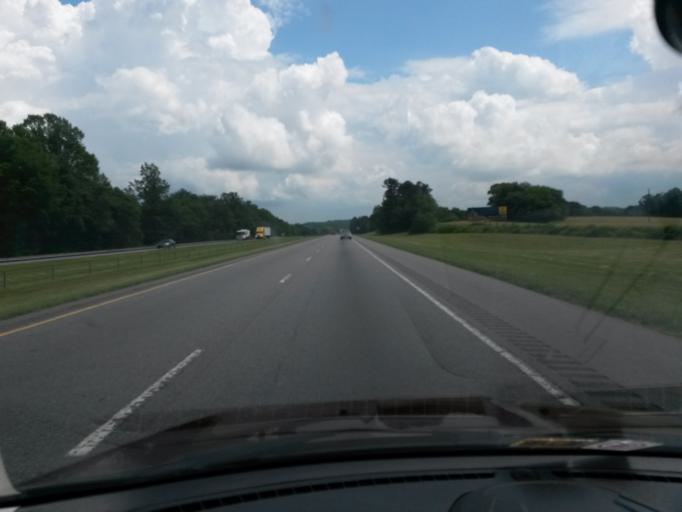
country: US
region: North Carolina
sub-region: Yadkin County
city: Yadkinville
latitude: 36.0439
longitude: -80.8212
